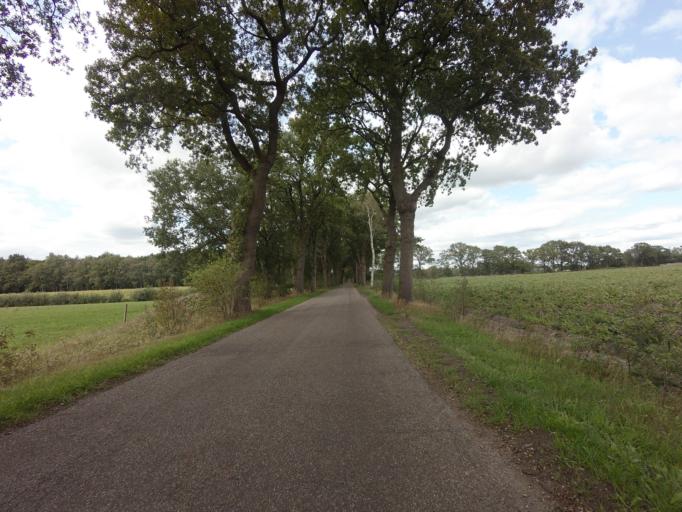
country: NL
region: Drenthe
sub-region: Gemeente De Wolden
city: Ruinen
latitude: 52.7344
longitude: 6.3433
